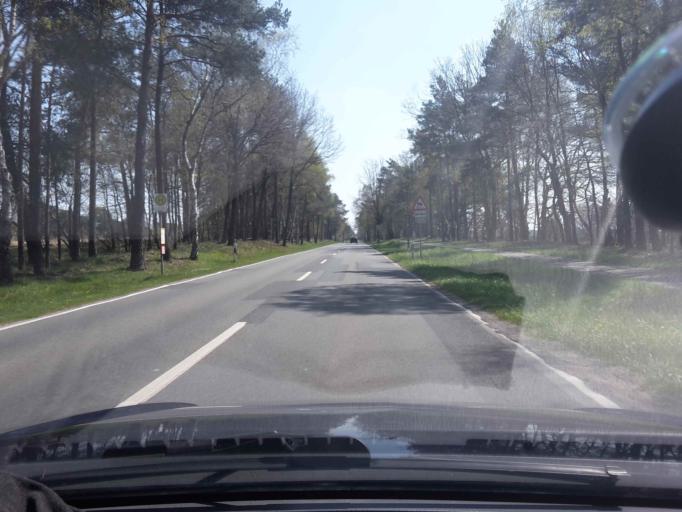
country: DE
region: Lower Saxony
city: Schneverdingen
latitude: 53.1063
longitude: 9.8189
